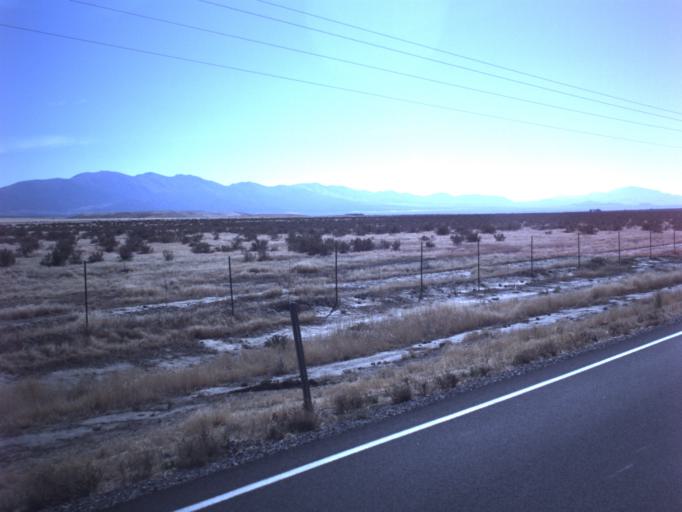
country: US
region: Utah
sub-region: Tooele County
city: Grantsville
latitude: 40.3730
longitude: -112.7465
